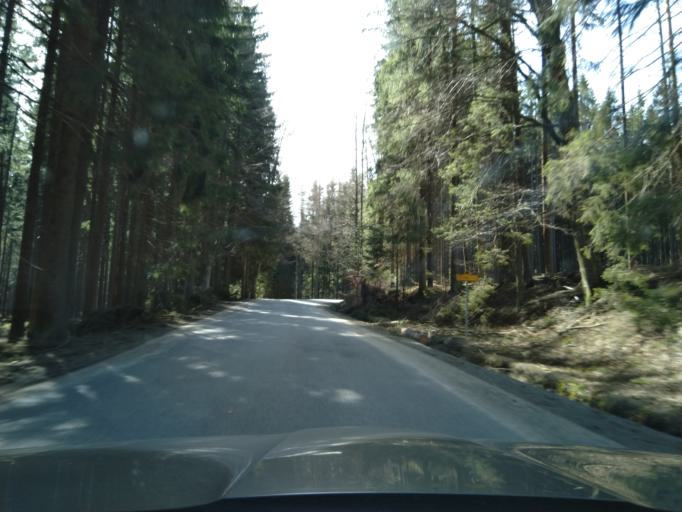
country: CZ
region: Jihocesky
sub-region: Okres Prachatice
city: Stachy
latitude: 49.0576
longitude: 13.6562
